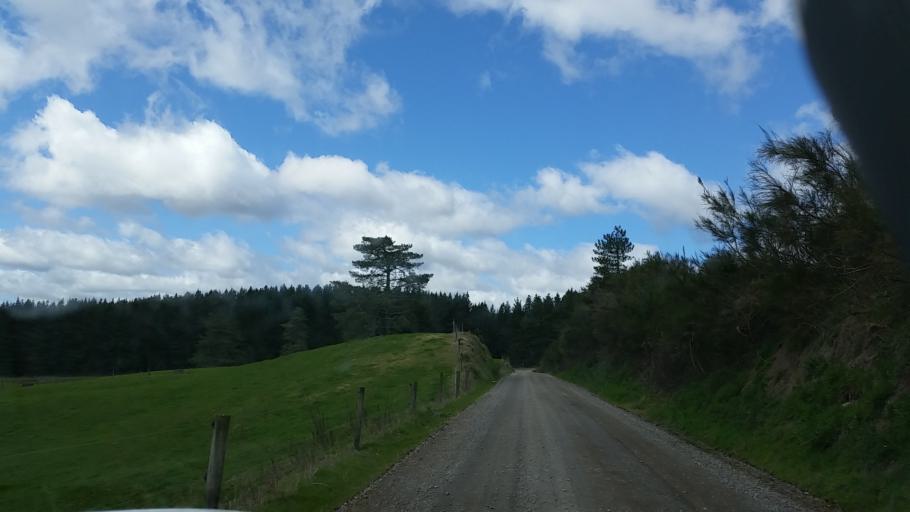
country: NZ
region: Bay of Plenty
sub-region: Whakatane District
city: Murupara
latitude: -38.3431
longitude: 176.5420
